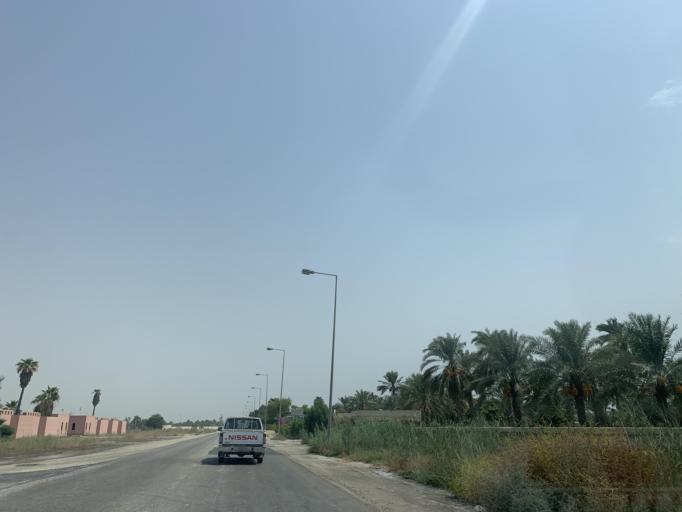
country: BH
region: Central Governorate
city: Madinat Hamad
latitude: 26.1609
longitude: 50.4660
